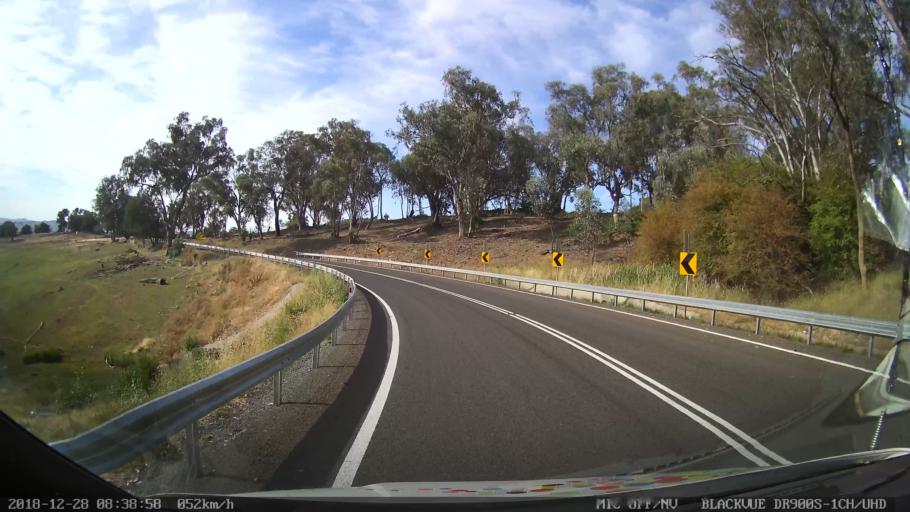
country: AU
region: New South Wales
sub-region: Upper Lachlan Shire
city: Crookwell
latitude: -34.0084
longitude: 149.3166
